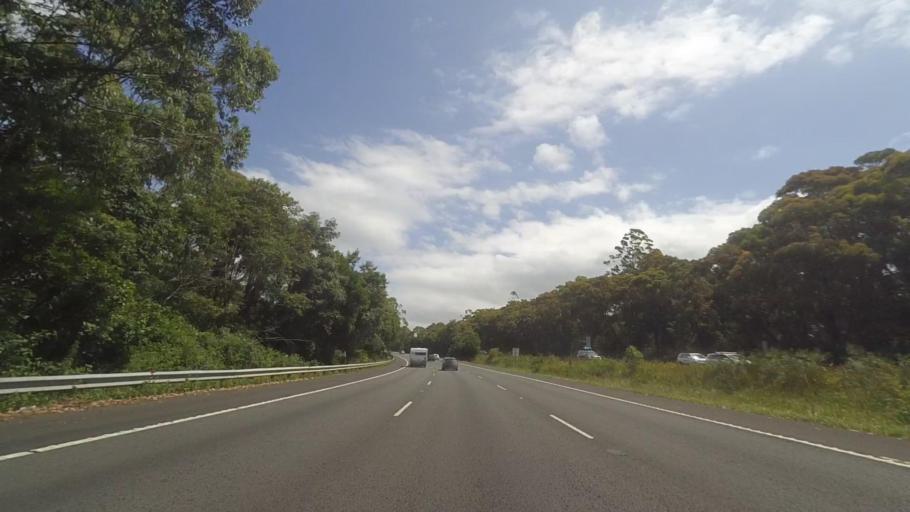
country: AU
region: New South Wales
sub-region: Gosford Shire
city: Lisarow
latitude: -33.3611
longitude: 151.3352
